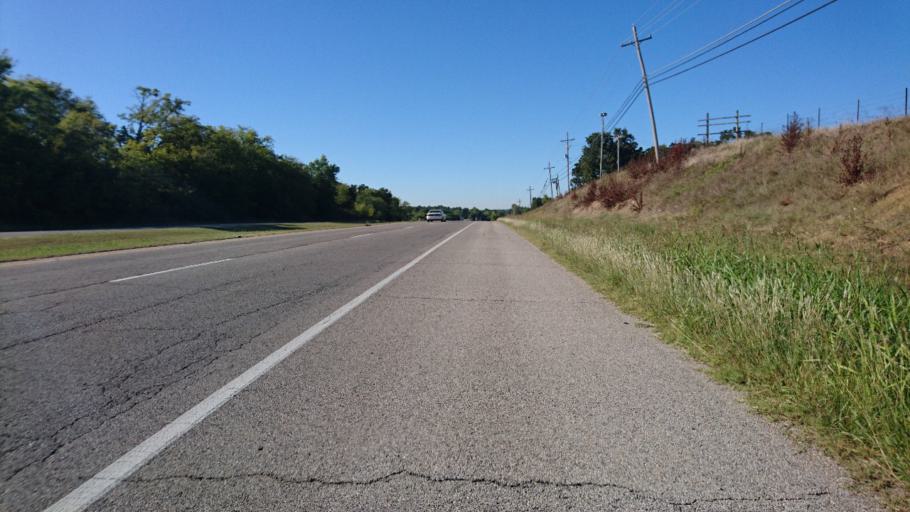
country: US
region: Oklahoma
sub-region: Rogers County
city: Catoosa
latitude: 36.2014
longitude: -95.7282
